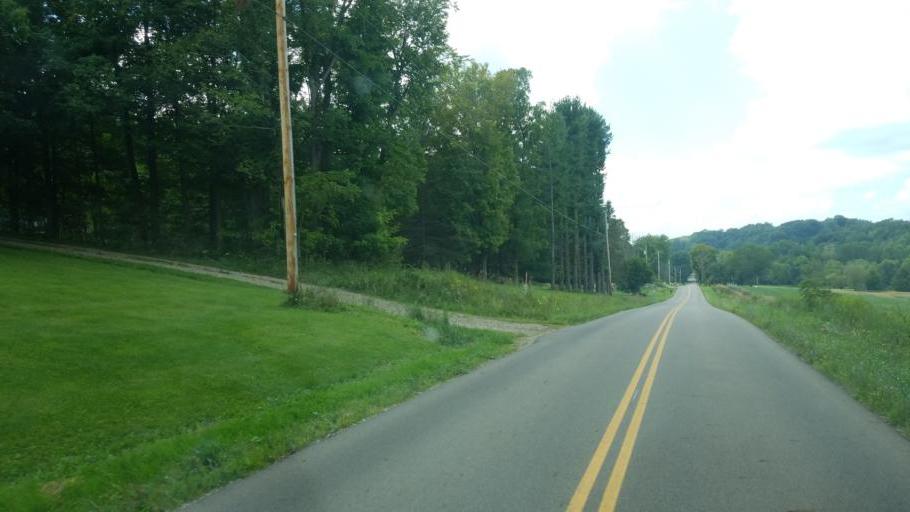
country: US
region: Ohio
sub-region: Knox County
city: Gambier
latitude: 40.4284
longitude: -82.4324
